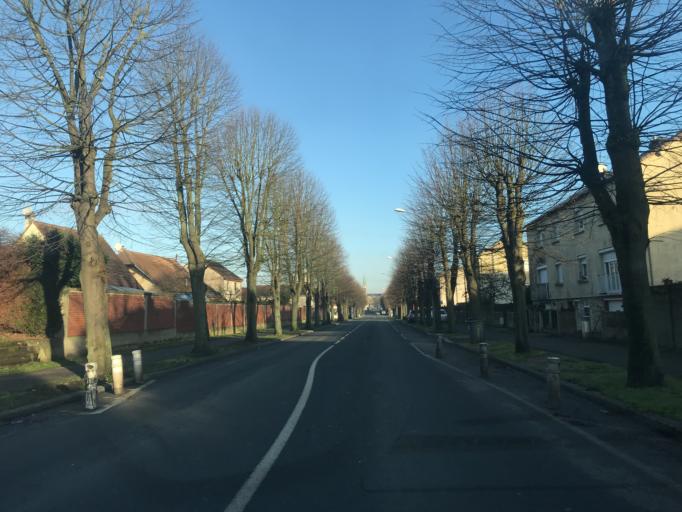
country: FR
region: Haute-Normandie
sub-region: Departement de la Seine-Maritime
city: Sotteville-les-Rouen
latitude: 49.4101
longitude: 1.1003
